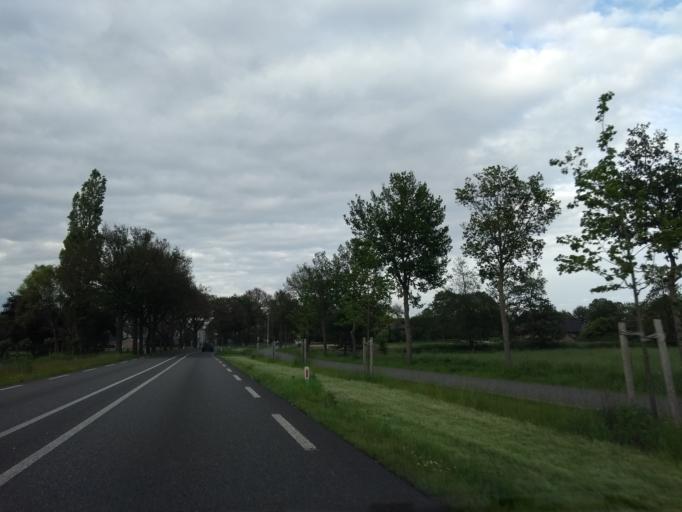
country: NL
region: Gelderland
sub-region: Berkelland
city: Borculo
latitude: 52.1207
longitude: 6.5477
